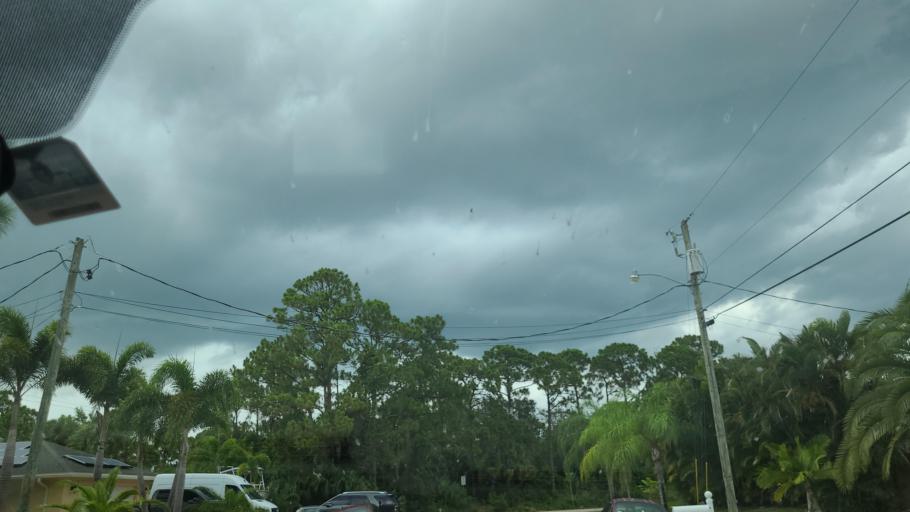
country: US
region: Florida
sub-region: Saint Lucie County
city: Port Saint Lucie
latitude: 27.2523
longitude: -80.4147
